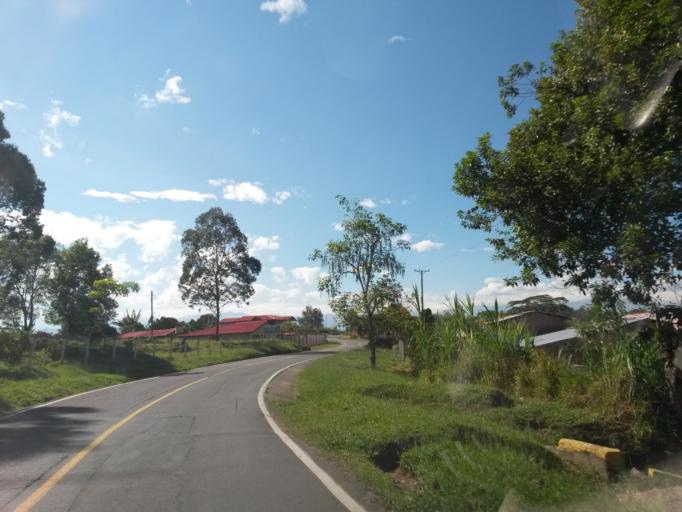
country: CO
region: Cauca
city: Morales
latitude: 2.7457
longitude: -76.6218
